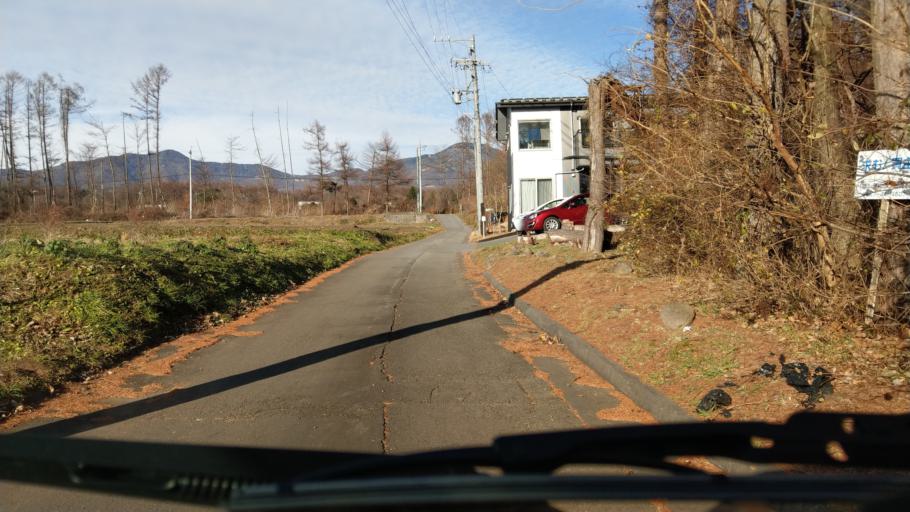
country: JP
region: Nagano
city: Komoro
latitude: 36.3426
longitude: 138.4620
